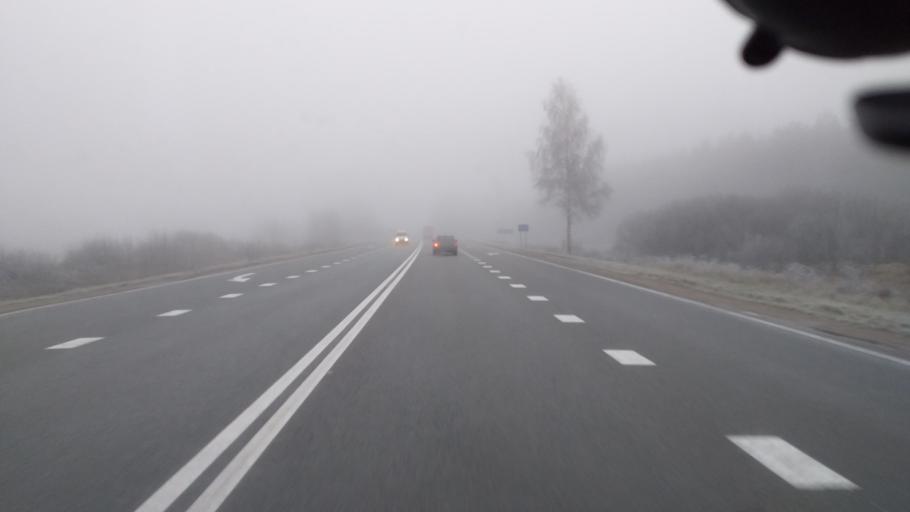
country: LV
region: Marupe
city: Marupe
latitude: 56.8394
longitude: 24.0267
